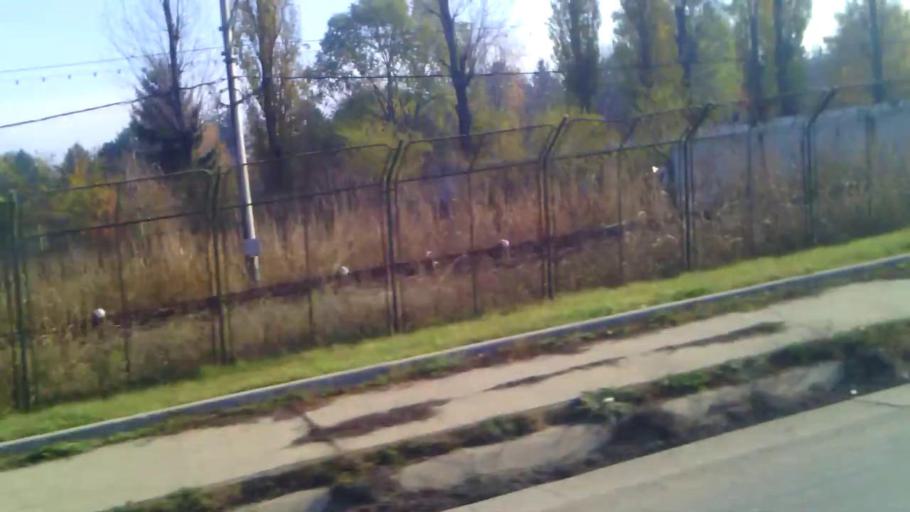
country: RO
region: Ilfov
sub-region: Comuna Berceni
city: Berceni
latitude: 44.3443
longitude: 26.1620
